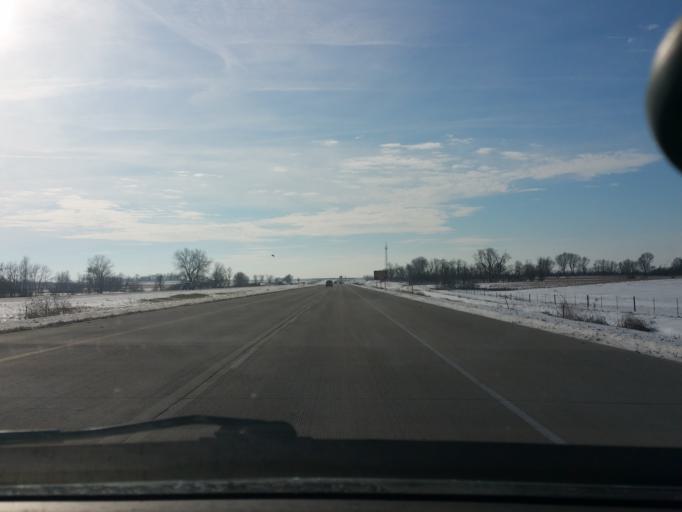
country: US
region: Iowa
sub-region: Polk County
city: West Des Moines
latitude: 41.5002
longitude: -93.7805
